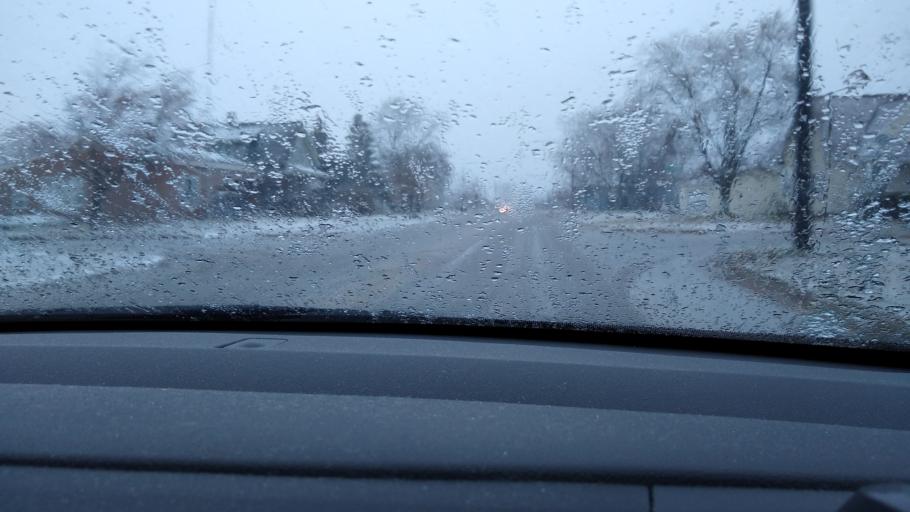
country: US
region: Michigan
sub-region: Delta County
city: Escanaba
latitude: 45.7478
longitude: -87.0612
